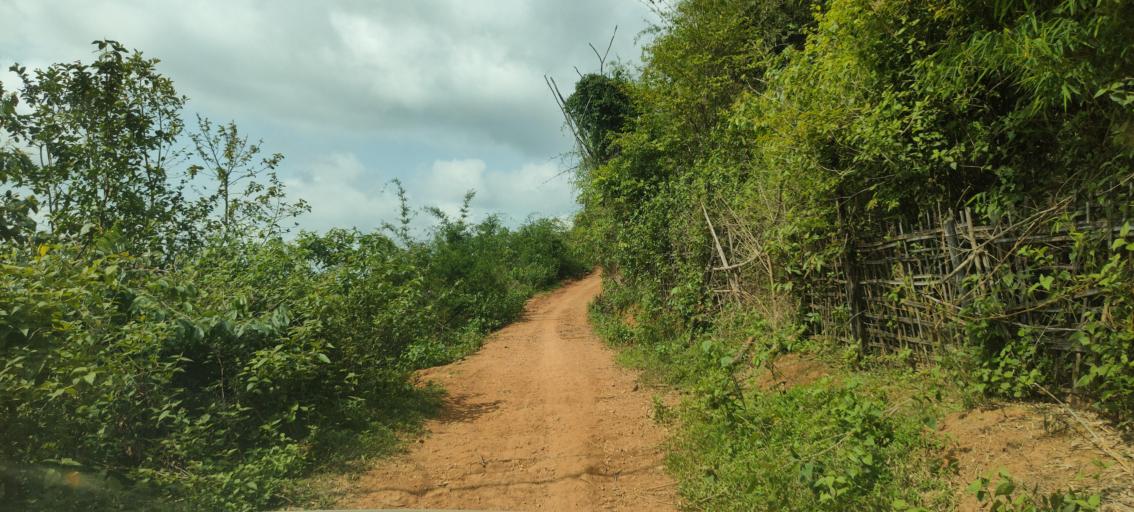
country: LA
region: Loungnamtha
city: Muang Nale
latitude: 20.4276
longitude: 101.4699
